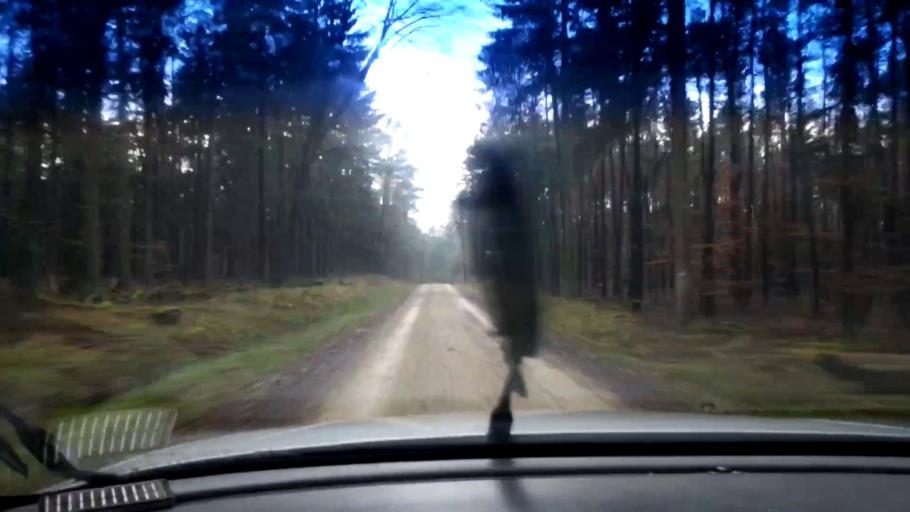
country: DE
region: Bavaria
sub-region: Upper Franconia
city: Gundelsheim
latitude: 49.9553
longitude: 10.9039
